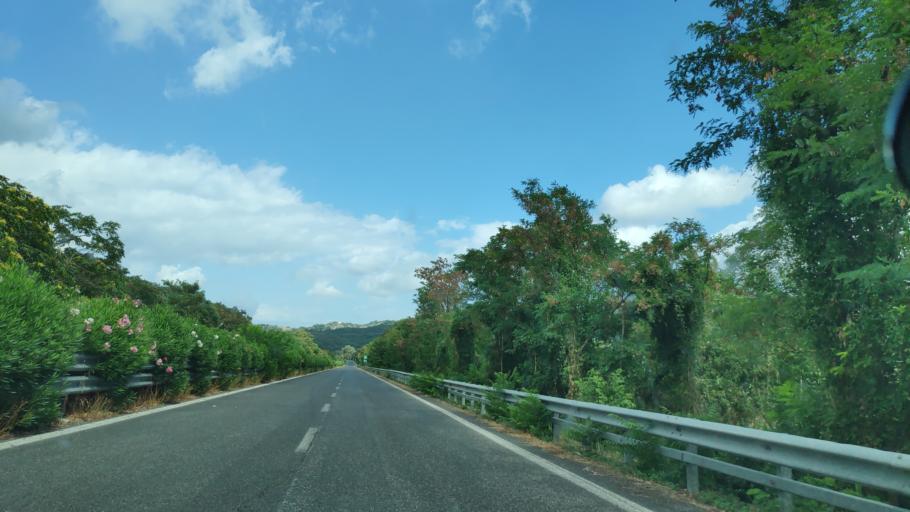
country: IT
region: Campania
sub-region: Provincia di Salerno
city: Serre
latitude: 40.6167
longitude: 15.1680
